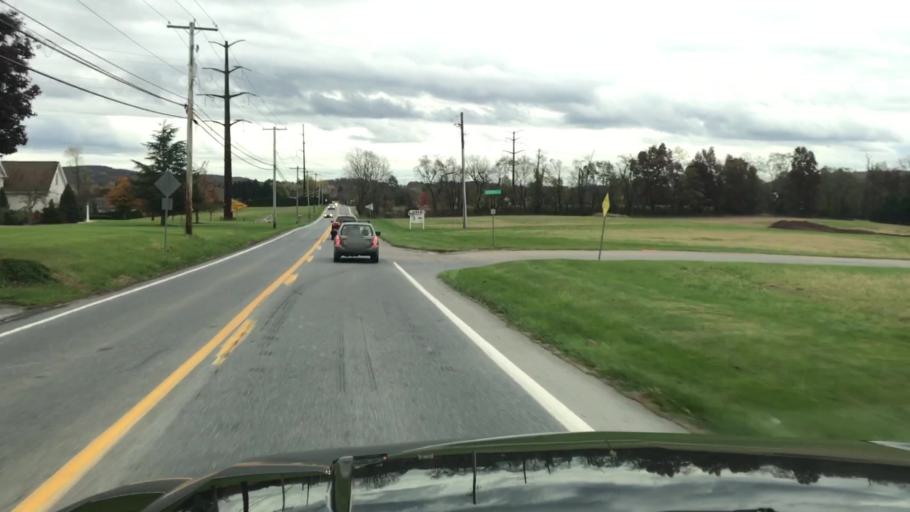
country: US
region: Pennsylvania
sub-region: Cumberland County
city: Shiremanstown
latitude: 40.1720
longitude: -76.9315
